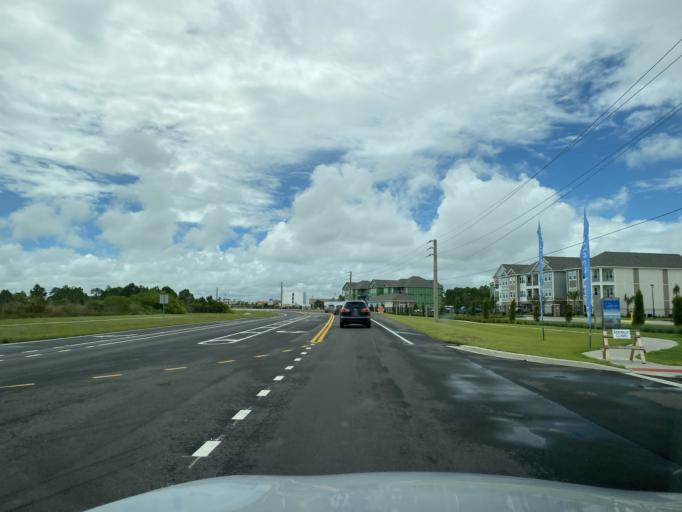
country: US
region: Florida
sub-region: Brevard County
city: West Melbourne
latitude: 28.0426
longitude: -80.6544
